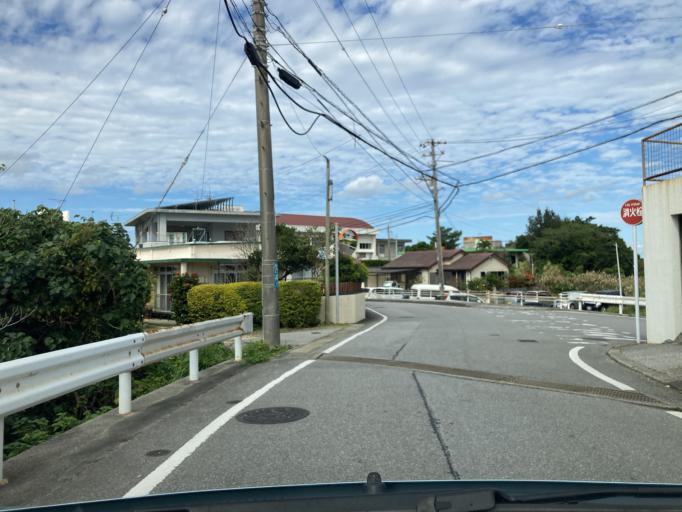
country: JP
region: Okinawa
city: Ishikawa
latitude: 26.4321
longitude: 127.7786
